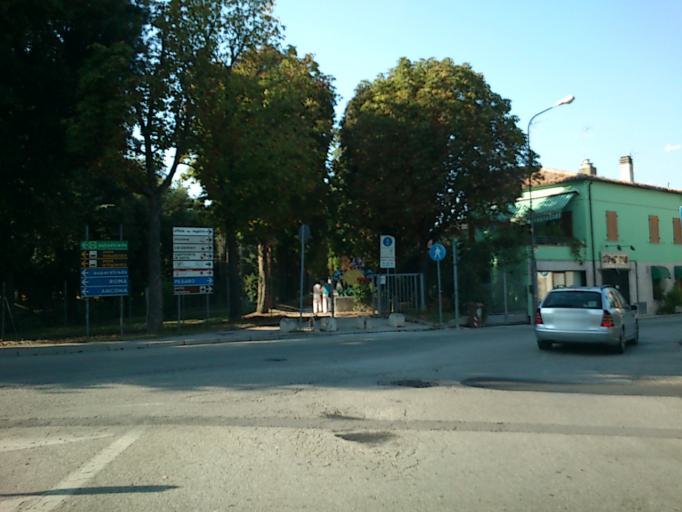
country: IT
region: The Marches
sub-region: Provincia di Pesaro e Urbino
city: Fano
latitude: 43.8373
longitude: 13.0133
